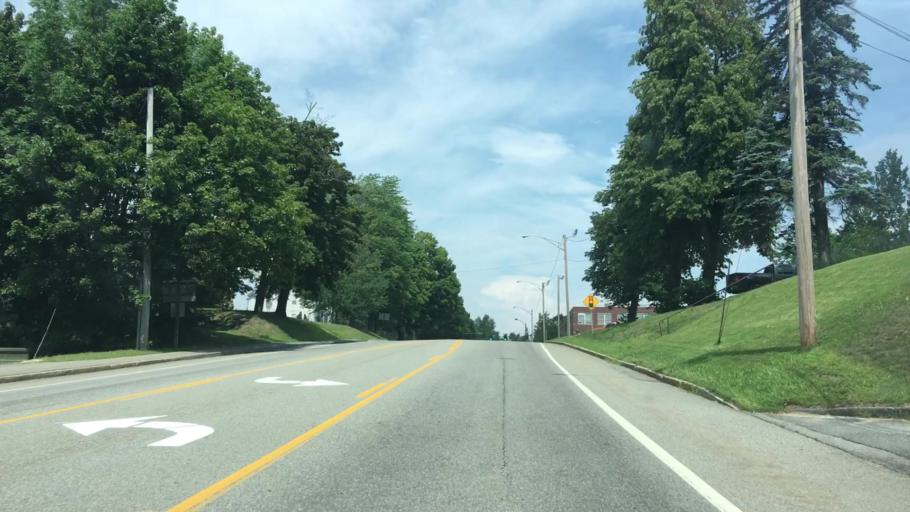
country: US
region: Maine
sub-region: Kennebec County
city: Augusta
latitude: 44.3039
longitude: -69.7817
